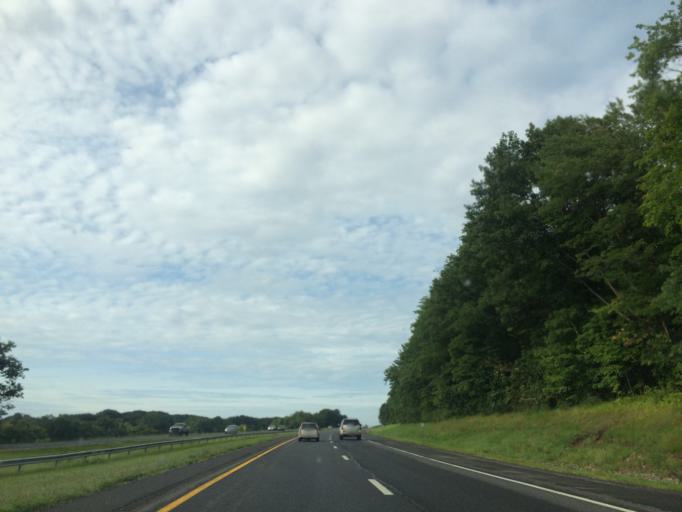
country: US
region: New York
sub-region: Ulster County
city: Lake Katrine
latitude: 41.9901
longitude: -74.0061
